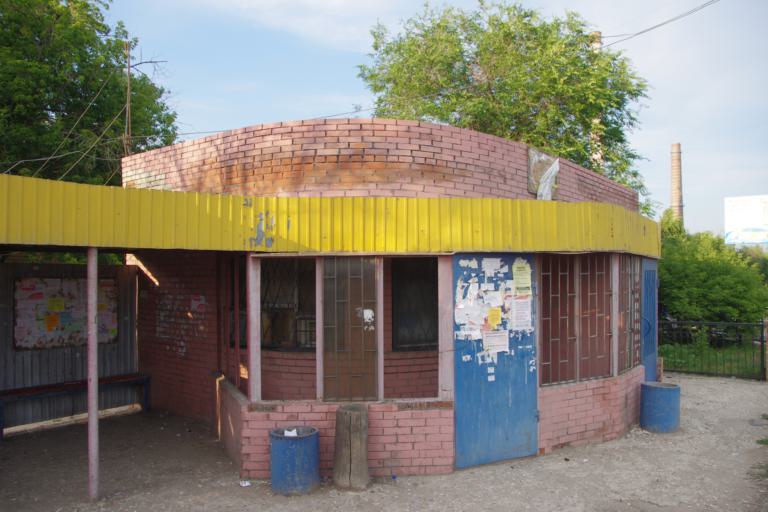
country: RU
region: Samara
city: Zhigulevsk
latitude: 53.4867
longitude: 49.4893
